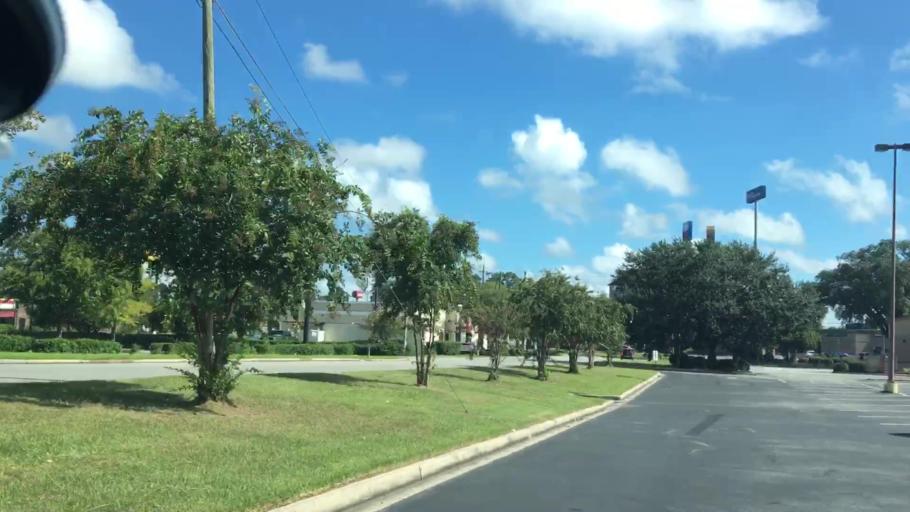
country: US
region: Georgia
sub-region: Lowndes County
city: Remerton
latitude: 30.8412
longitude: -83.3264
